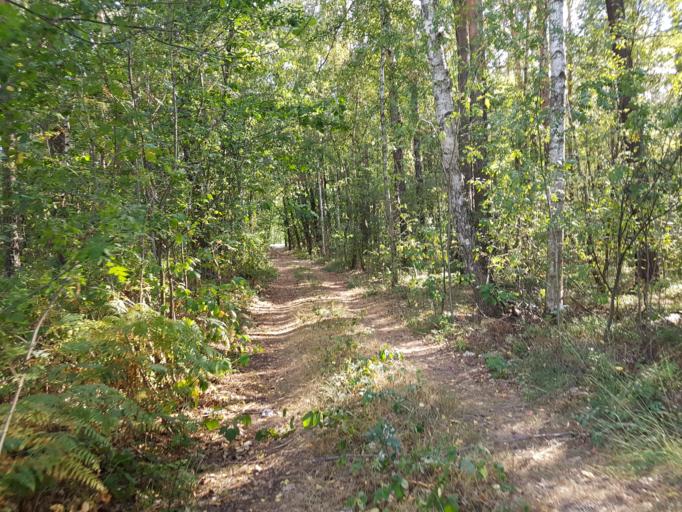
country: DE
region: Brandenburg
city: Doberlug-Kirchhain
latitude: 51.6314
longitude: 13.5952
